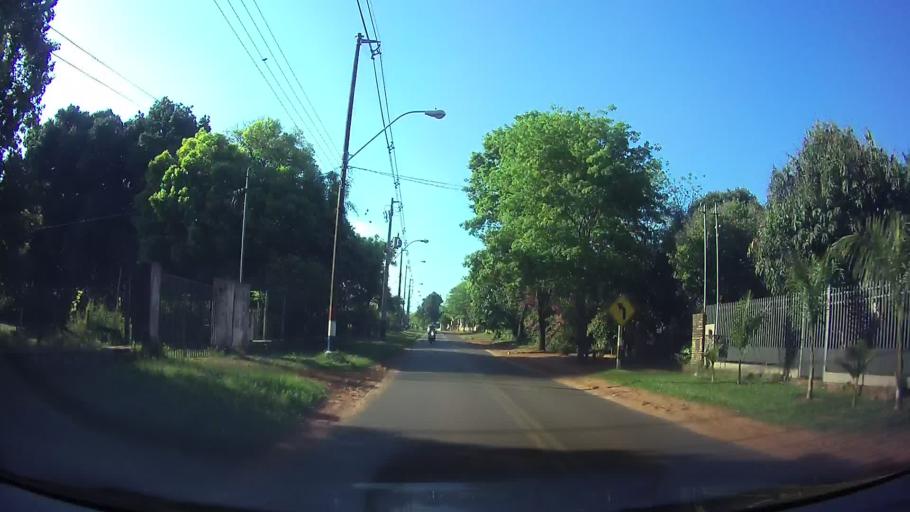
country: PY
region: Central
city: Capiata
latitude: -25.3116
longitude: -57.4330
